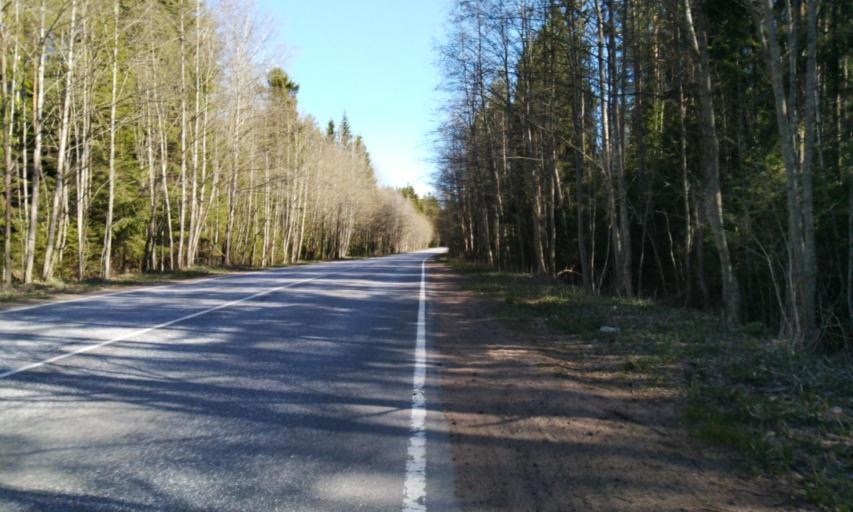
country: RU
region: Leningrad
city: Garbolovo
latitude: 60.3538
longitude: 30.4439
